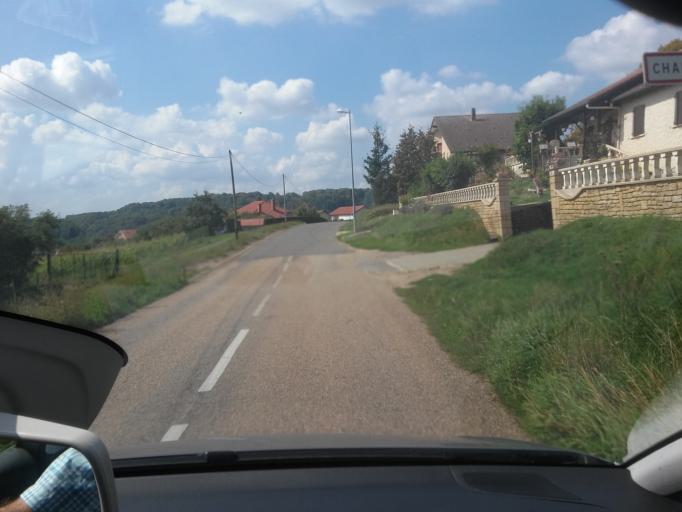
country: BE
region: Wallonia
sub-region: Province du Luxembourg
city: Rouvroy
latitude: 49.4901
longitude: 5.5162
